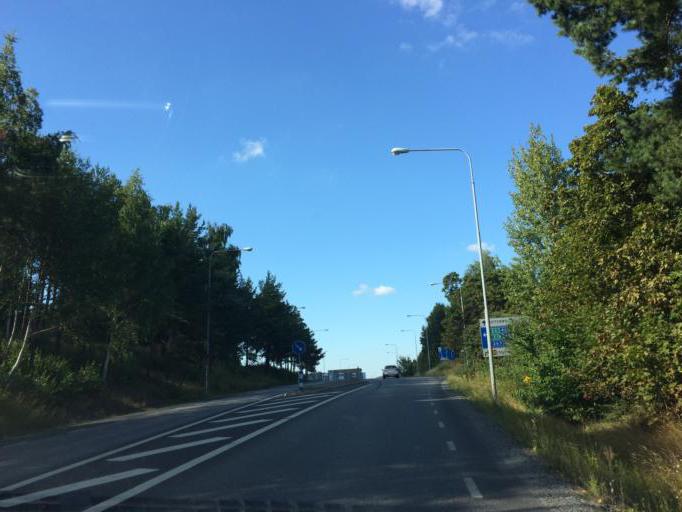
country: SE
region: Stockholm
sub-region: Sollentuna Kommun
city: Sollentuna
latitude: 59.4681
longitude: 17.9199
